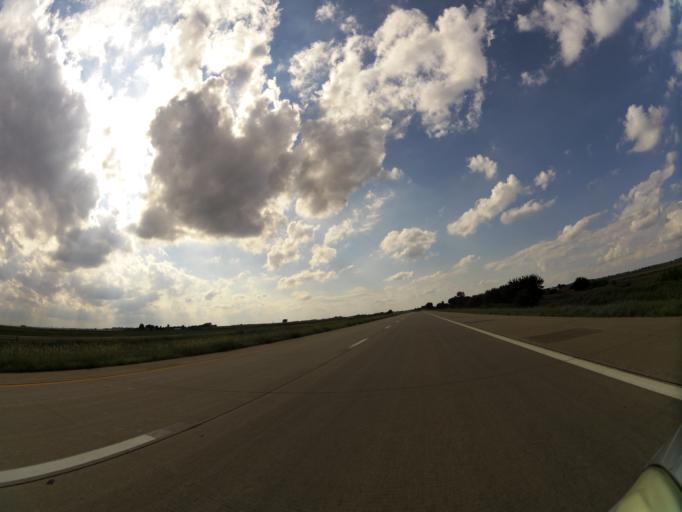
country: US
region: Kansas
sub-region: Sedgwick County
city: Colwich
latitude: 37.8344
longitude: -97.5663
